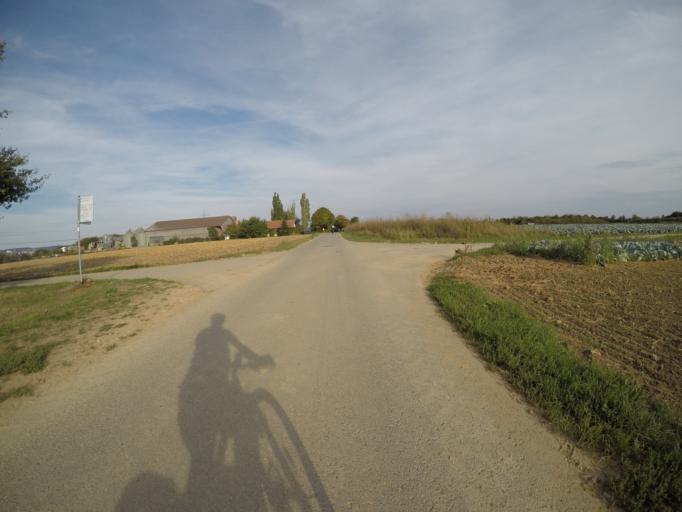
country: DE
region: Baden-Wuerttemberg
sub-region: Regierungsbezirk Stuttgart
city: Neuhausen auf den Fildern
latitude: 48.6977
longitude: 9.2802
